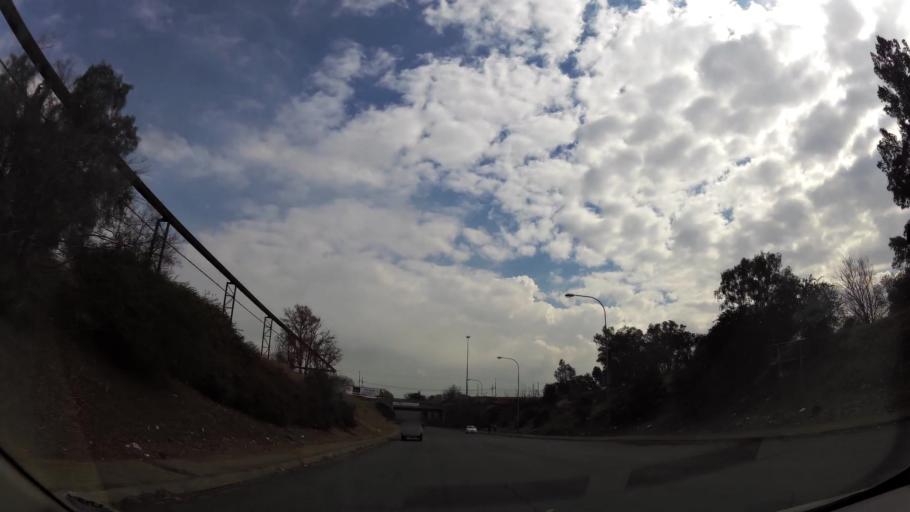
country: ZA
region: Gauteng
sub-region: Sedibeng District Municipality
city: Vereeniging
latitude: -26.6814
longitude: 27.9365
